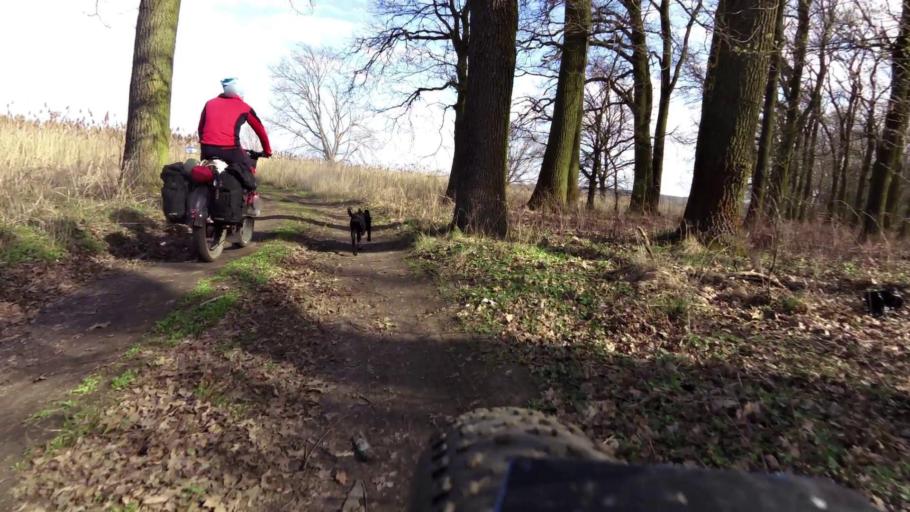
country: PL
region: Lubusz
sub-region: Powiat slubicki
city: Slubice
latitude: 52.3335
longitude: 14.5648
